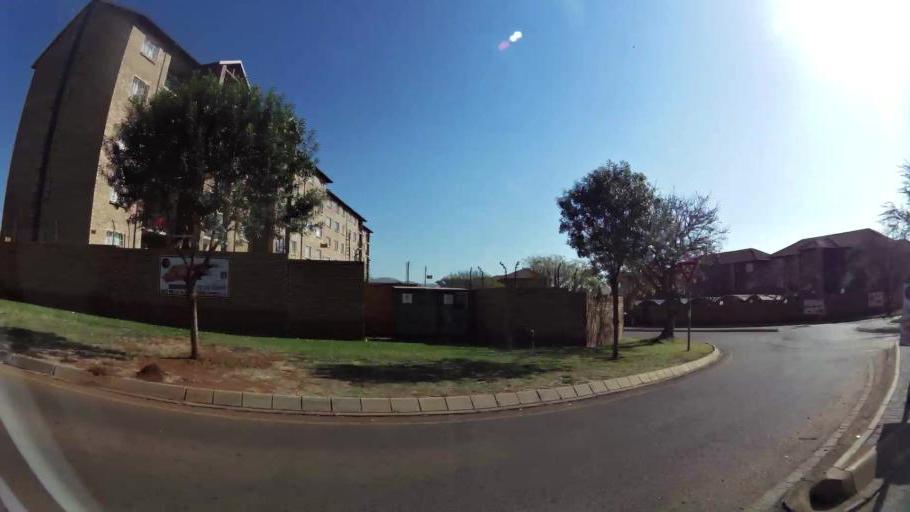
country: ZA
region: Gauteng
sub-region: City of Tshwane Metropolitan Municipality
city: Pretoria
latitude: -25.6768
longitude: 28.1906
